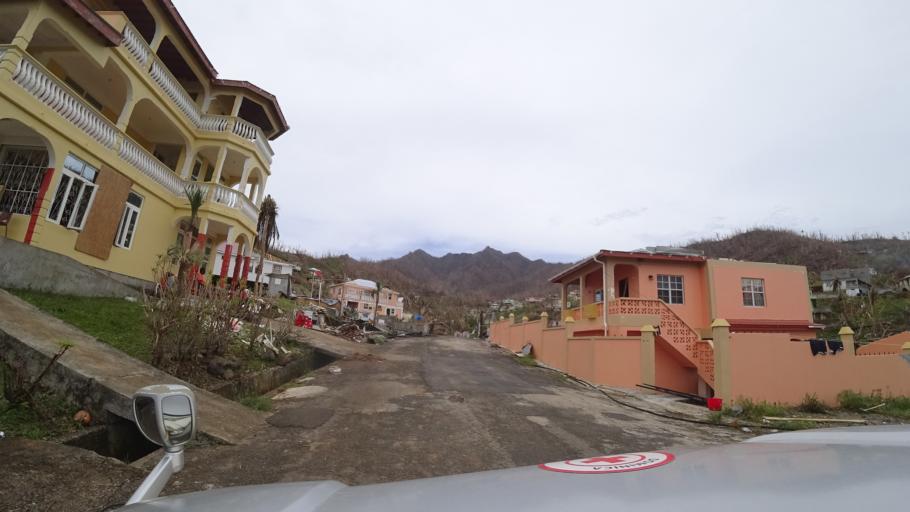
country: DM
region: Saint David
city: Castle Bruce
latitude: 15.4413
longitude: -61.2574
